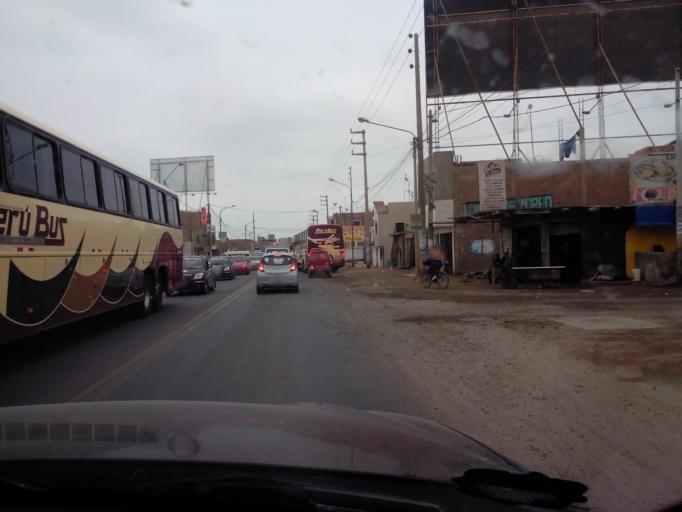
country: PE
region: Ica
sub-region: Provincia de Chincha
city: Chincha Alta
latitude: -13.4156
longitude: -76.1424
